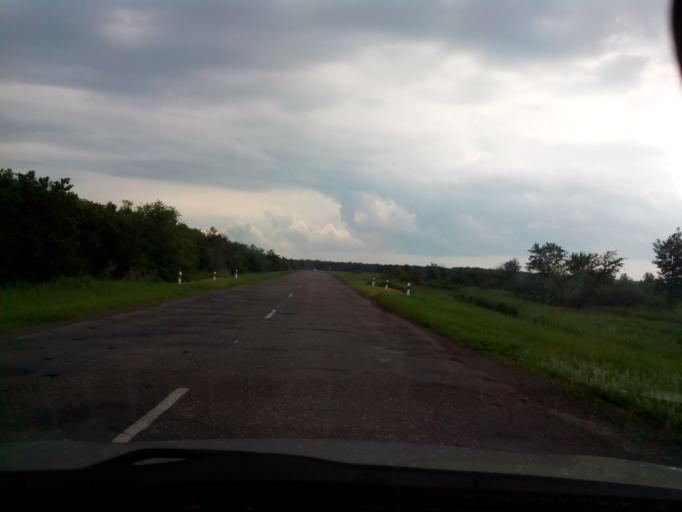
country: RU
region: Volgograd
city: Kumylzhenskaya
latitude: 49.9027
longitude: 42.8384
